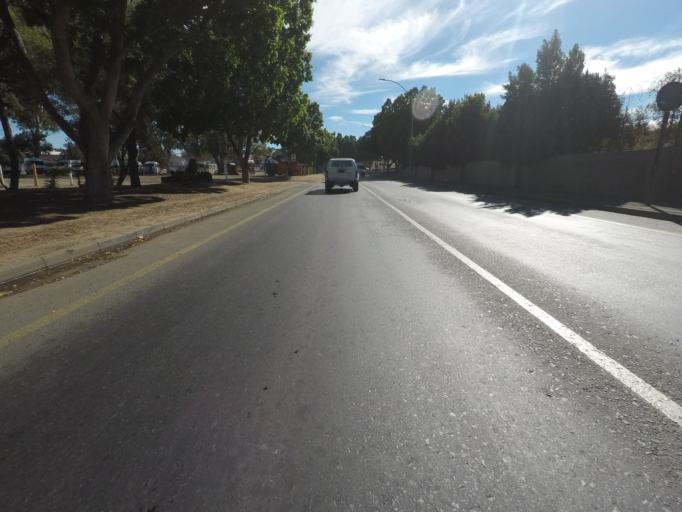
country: ZA
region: Western Cape
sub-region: West Coast District Municipality
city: Malmesbury
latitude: -33.4676
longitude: 18.7281
